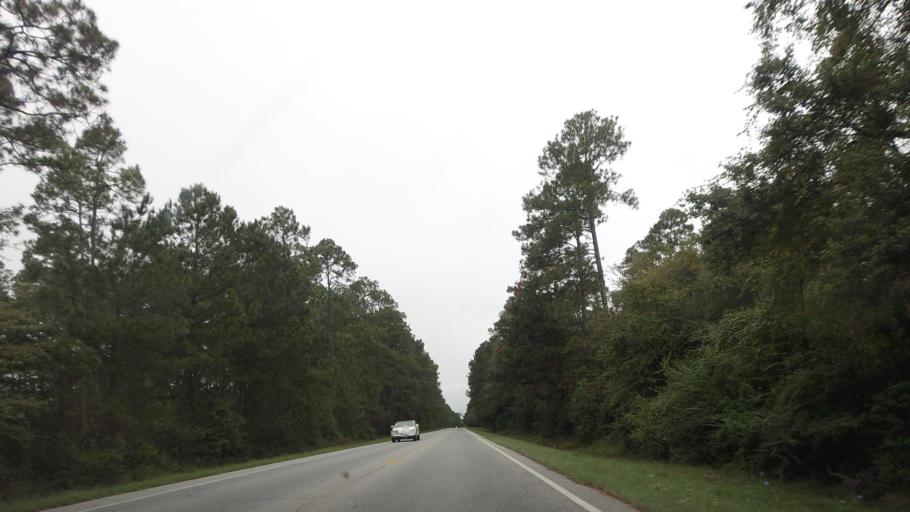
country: US
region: Georgia
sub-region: Berrien County
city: Nashville
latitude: 31.1856
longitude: -83.2434
